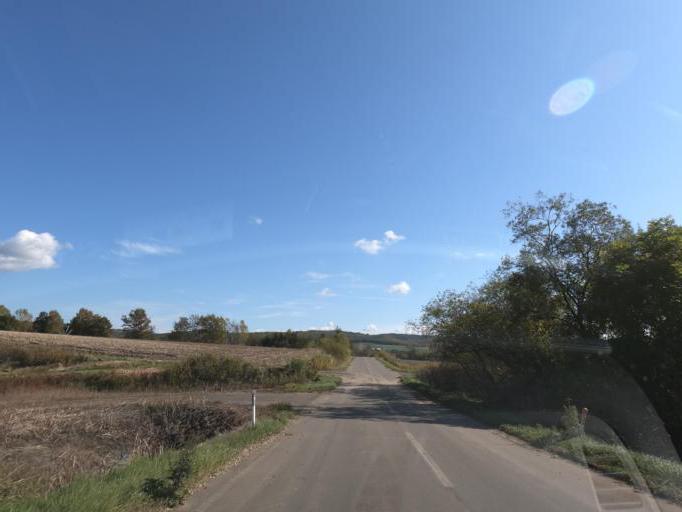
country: JP
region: Hokkaido
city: Otofuke
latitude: 43.0600
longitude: 143.2720
